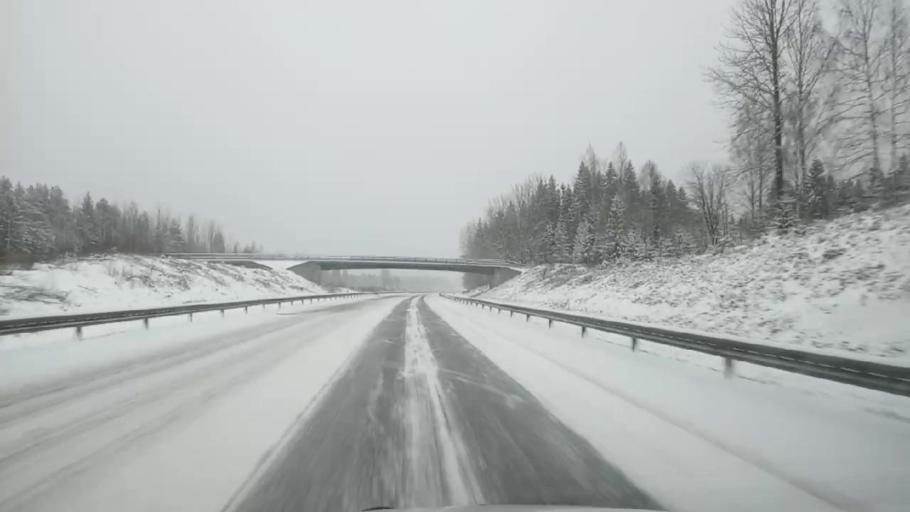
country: SE
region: Gaevleborg
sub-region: Gavle Kommun
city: Gavle
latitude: 60.5528
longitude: 17.2570
